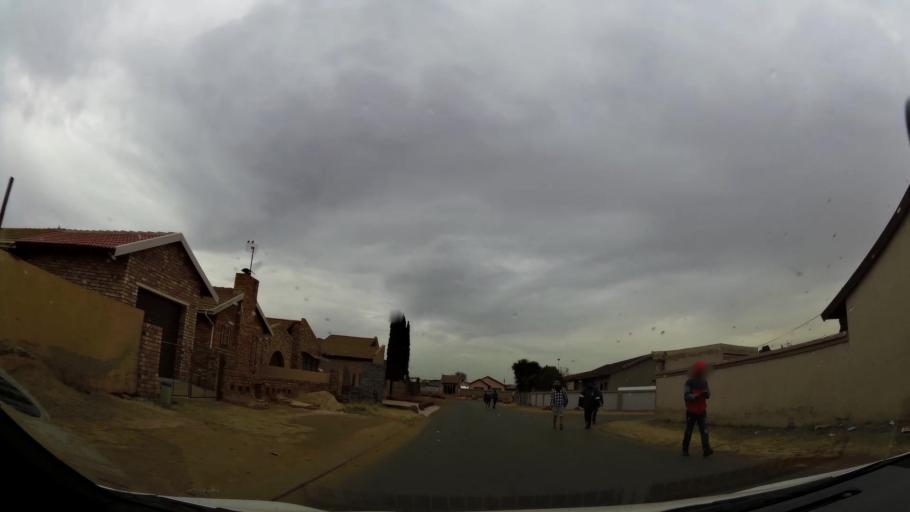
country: ZA
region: Gauteng
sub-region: Ekurhuleni Metropolitan Municipality
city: Germiston
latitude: -26.3778
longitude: 28.1575
